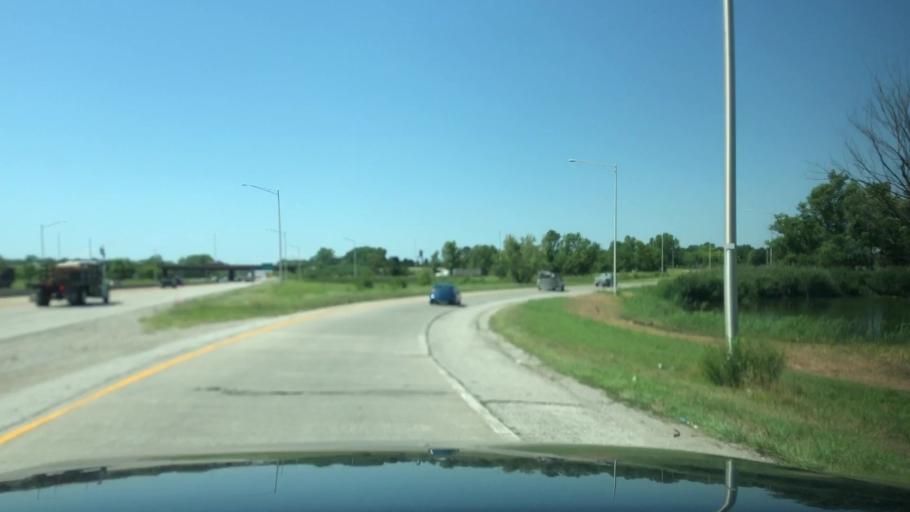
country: US
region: Illinois
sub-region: Saint Clair County
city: Alorton
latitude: 38.5797
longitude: -90.1044
